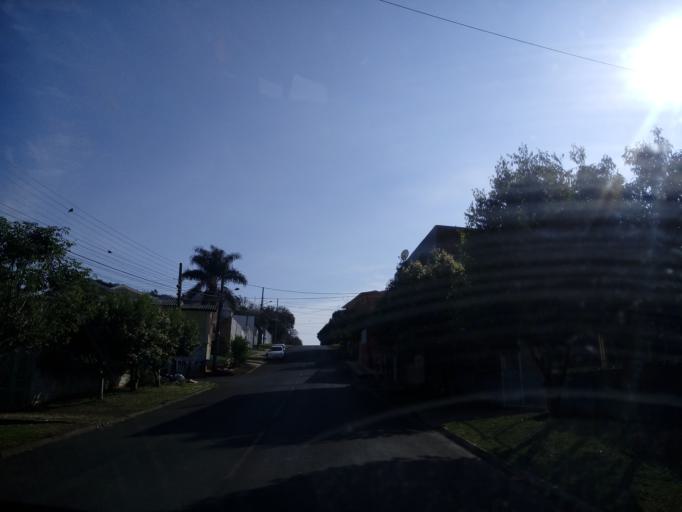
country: BR
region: Santa Catarina
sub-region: Chapeco
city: Chapeco
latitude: -27.1230
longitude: -52.6148
